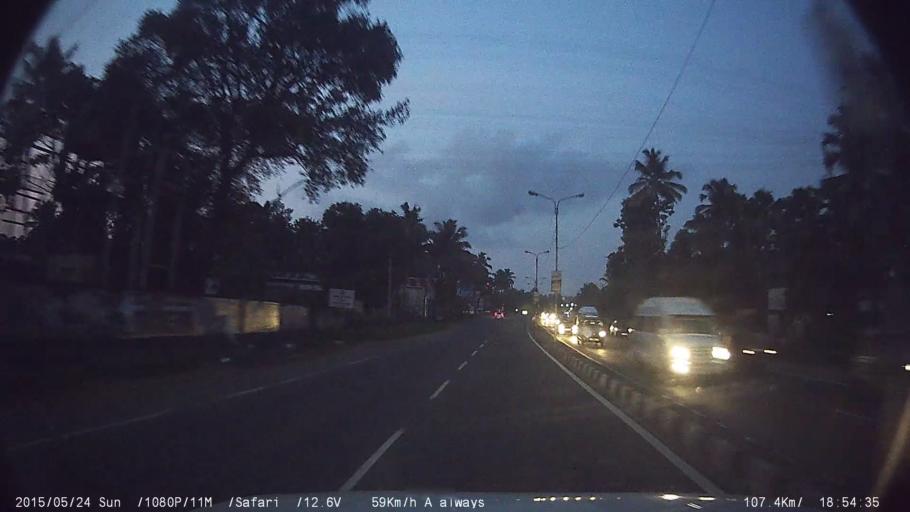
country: IN
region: Kerala
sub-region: Ernakulam
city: Angamali
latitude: 10.1721
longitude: 76.3735
